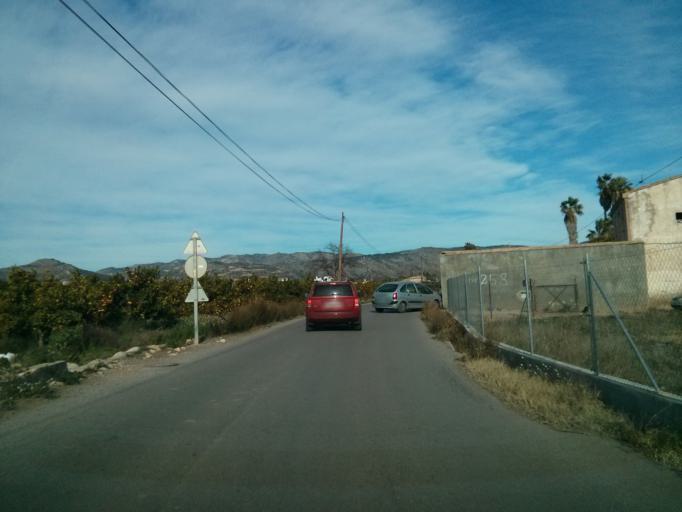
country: ES
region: Valencia
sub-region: Provincia de Castello
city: Castello de la Plana
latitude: 39.9933
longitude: -0.0203
